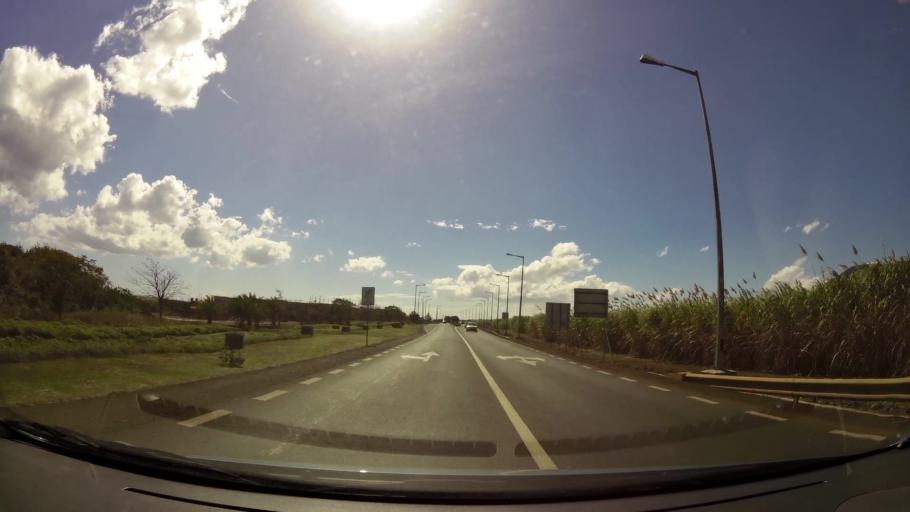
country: MU
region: Black River
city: Cascavelle
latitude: -20.2758
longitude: 57.4051
